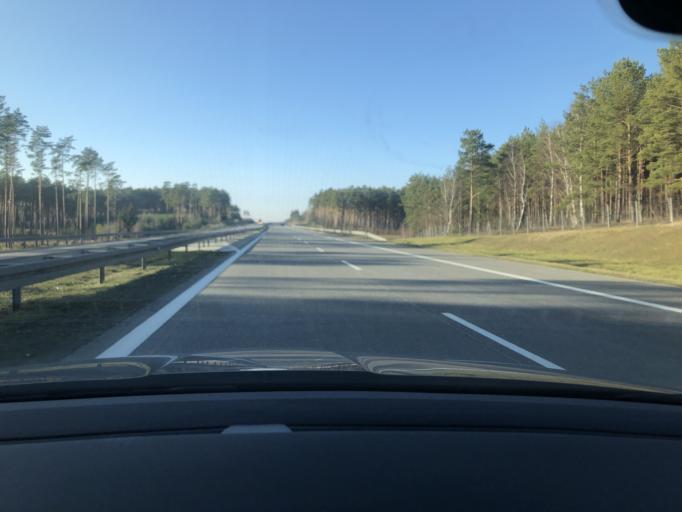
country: PL
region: Lubusz
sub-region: Powiat sulecinski
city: Torzym
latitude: 52.3270
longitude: 15.0489
